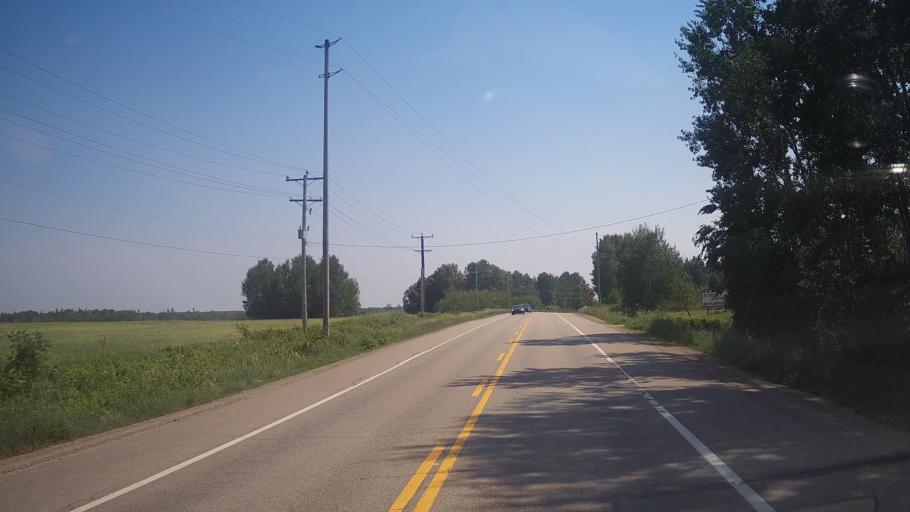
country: CA
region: Ontario
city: Pembroke
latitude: 45.8316
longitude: -77.0134
